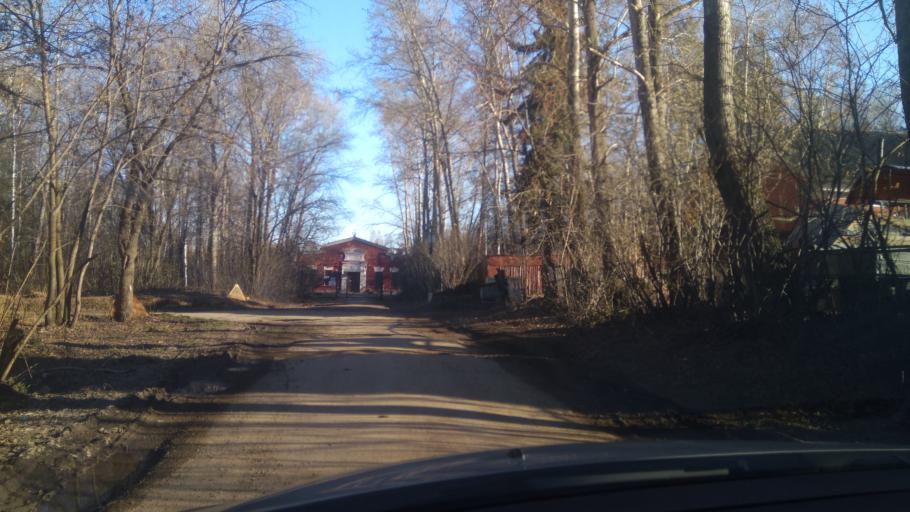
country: RU
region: Sverdlovsk
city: Verkhnyaya Pyshma
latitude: 56.9238
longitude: 60.6022
